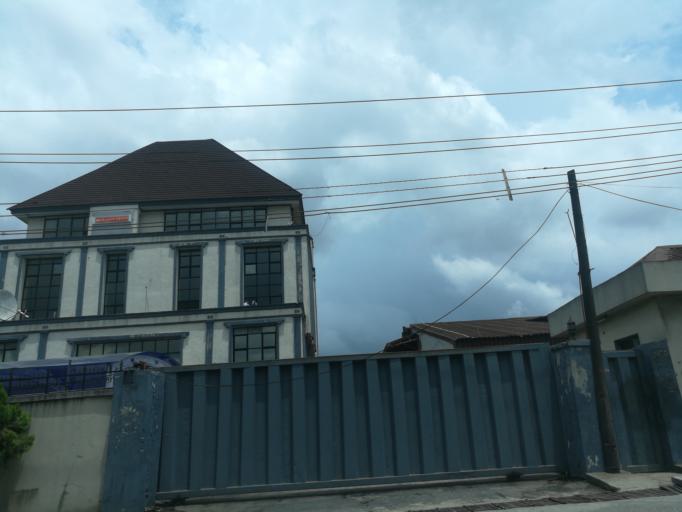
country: NG
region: Lagos
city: Oshodi
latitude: 6.5564
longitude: 3.3567
